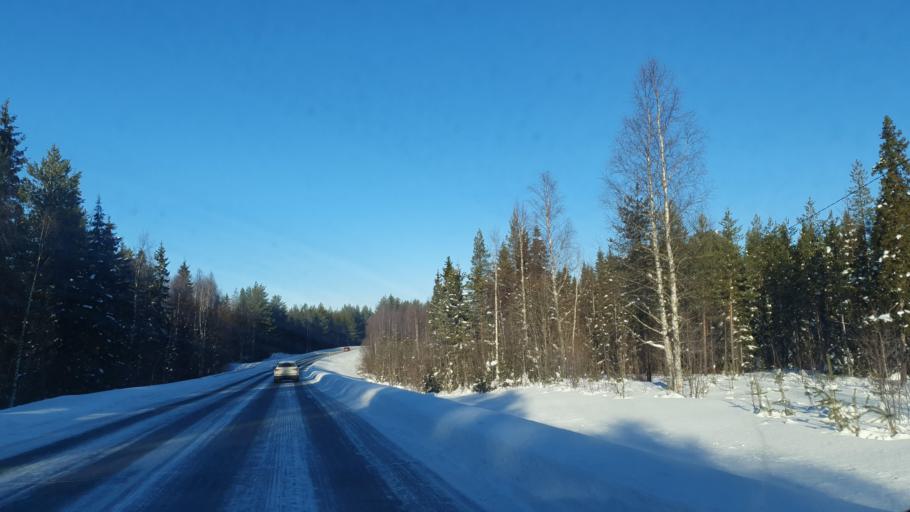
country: FI
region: Lapland
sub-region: Torniolaakso
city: Pello
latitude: 66.7114
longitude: 23.9051
